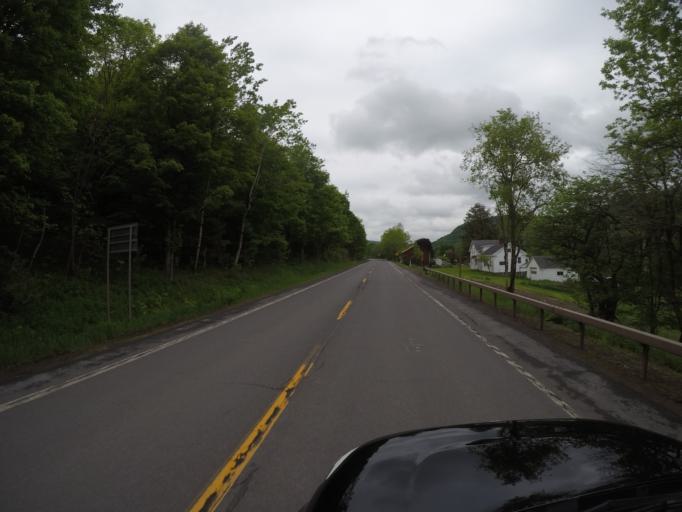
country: US
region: New York
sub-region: Delaware County
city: Delhi
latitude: 42.2551
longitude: -74.8970
